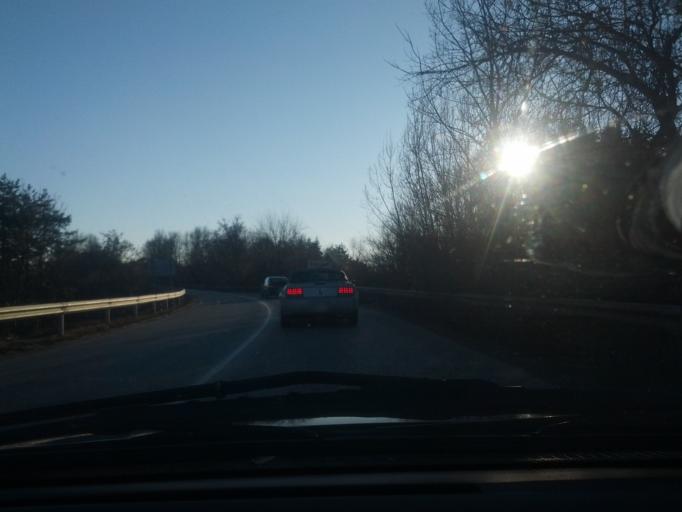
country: BG
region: Vratsa
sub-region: Obshtina Borovan
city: Borovan
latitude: 43.4172
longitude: 23.7393
